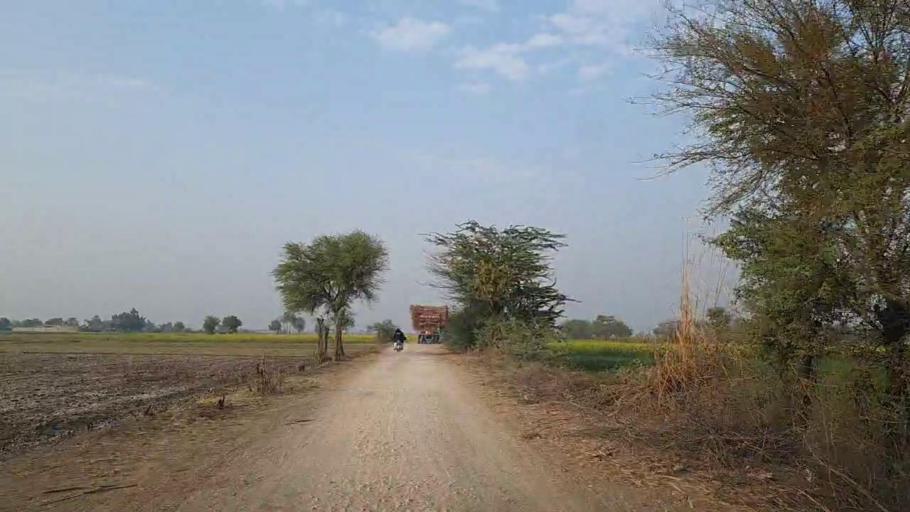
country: PK
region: Sindh
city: Jam Sahib
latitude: 26.3244
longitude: 68.5530
